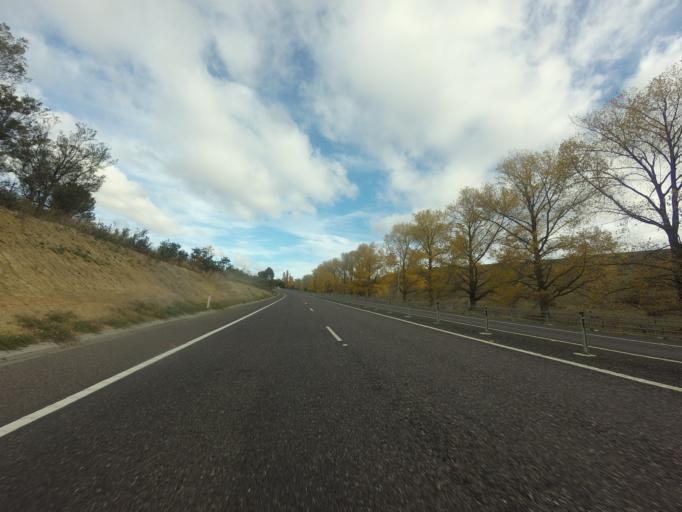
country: AU
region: Tasmania
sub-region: Brighton
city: Bridgewater
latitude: -42.5603
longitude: 147.2088
